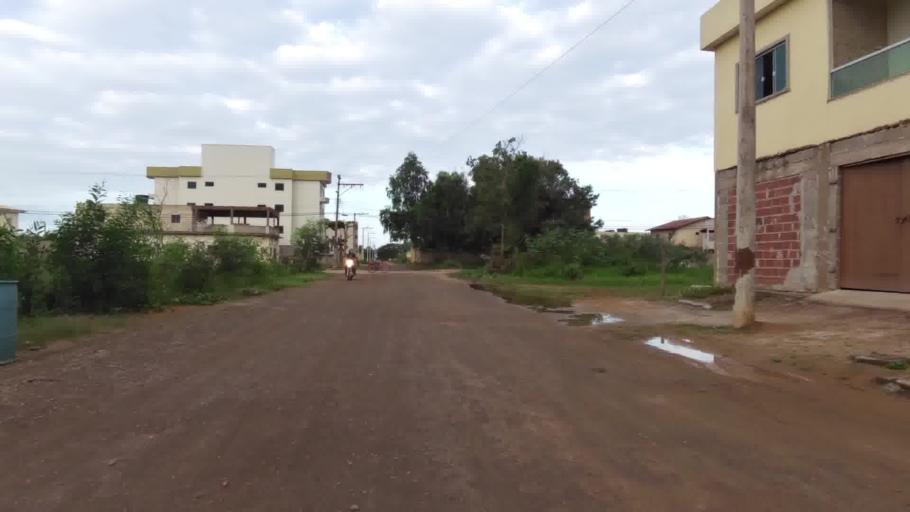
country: BR
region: Espirito Santo
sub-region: Piuma
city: Piuma
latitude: -20.8029
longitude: -40.6453
